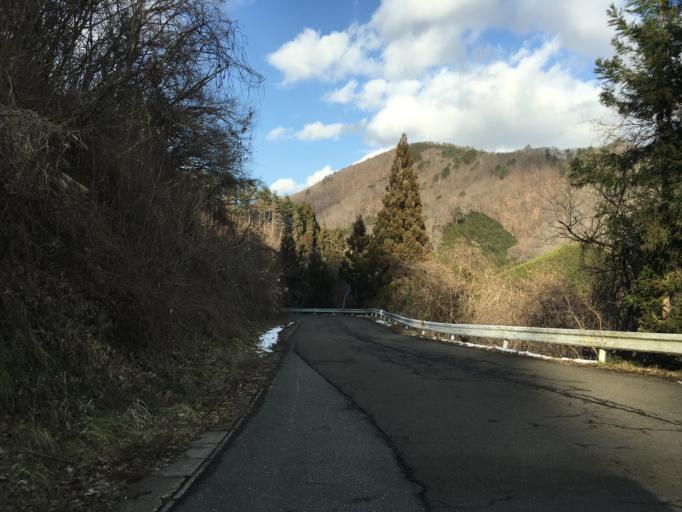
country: JP
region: Miyagi
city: Furukawa
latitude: 38.8127
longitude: 140.8326
